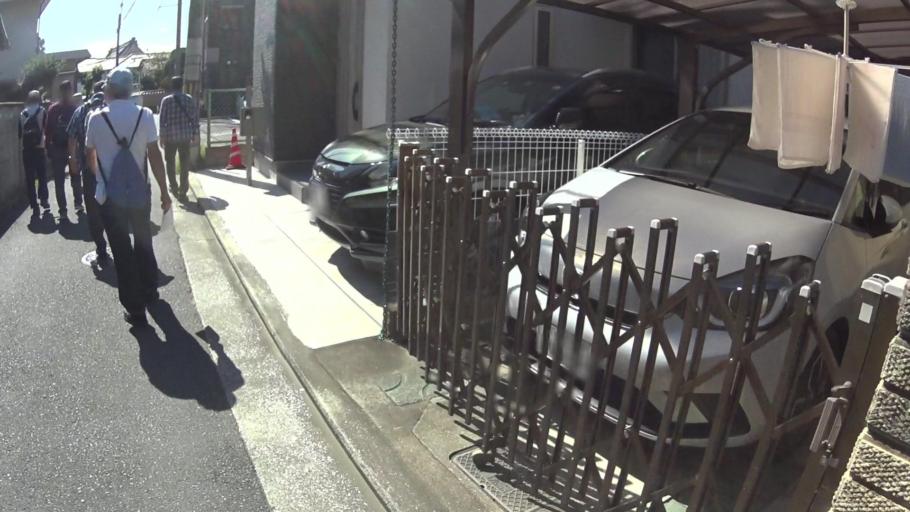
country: JP
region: Osaka
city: Sakai
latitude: 34.5445
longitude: 135.4691
